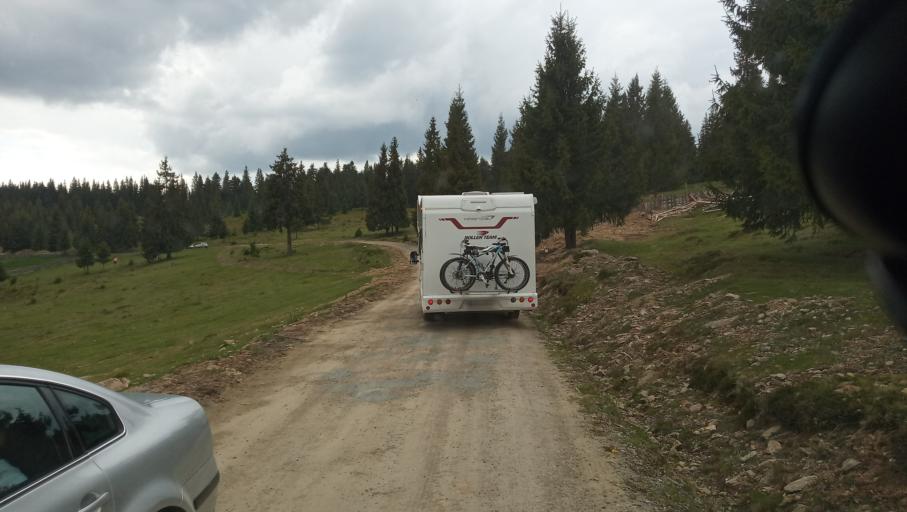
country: RO
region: Cluj
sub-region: Comuna Belis
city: Belis
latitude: 46.6360
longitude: 23.0443
